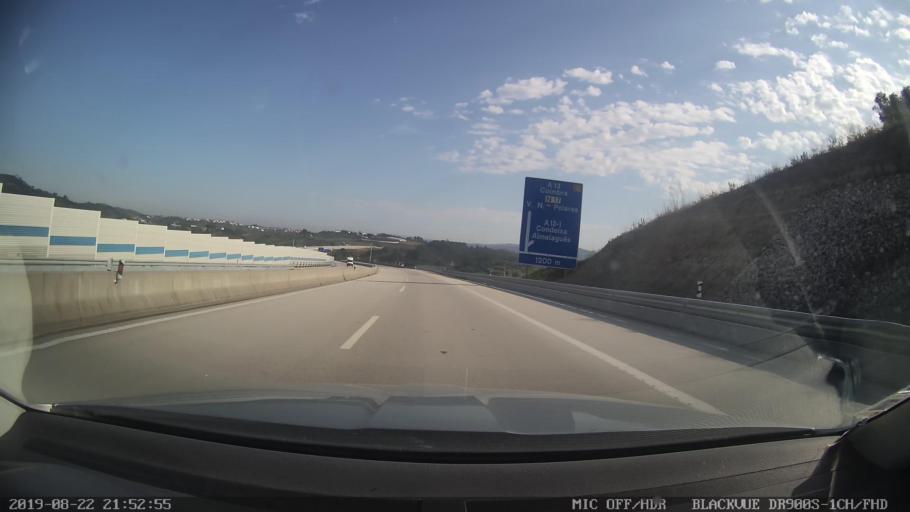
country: PT
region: Coimbra
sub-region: Miranda do Corvo
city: Miranda do Corvo
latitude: 40.1073
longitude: -8.3905
